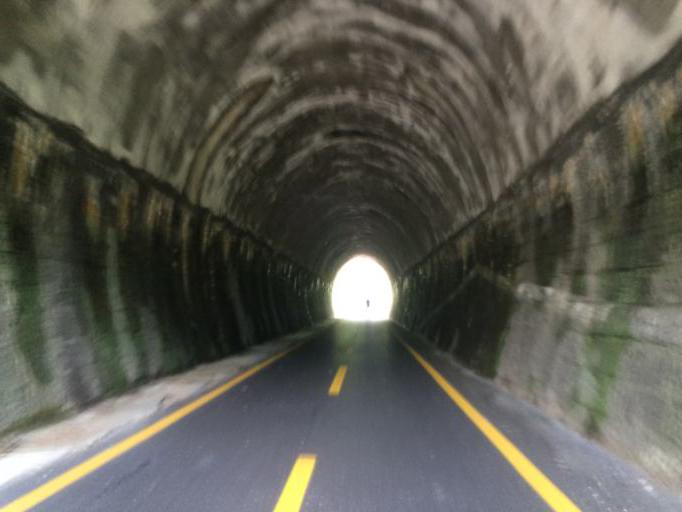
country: IT
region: Friuli Venezia Giulia
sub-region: Provincia di Udine
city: Dogna
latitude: 46.4566
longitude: 13.3098
